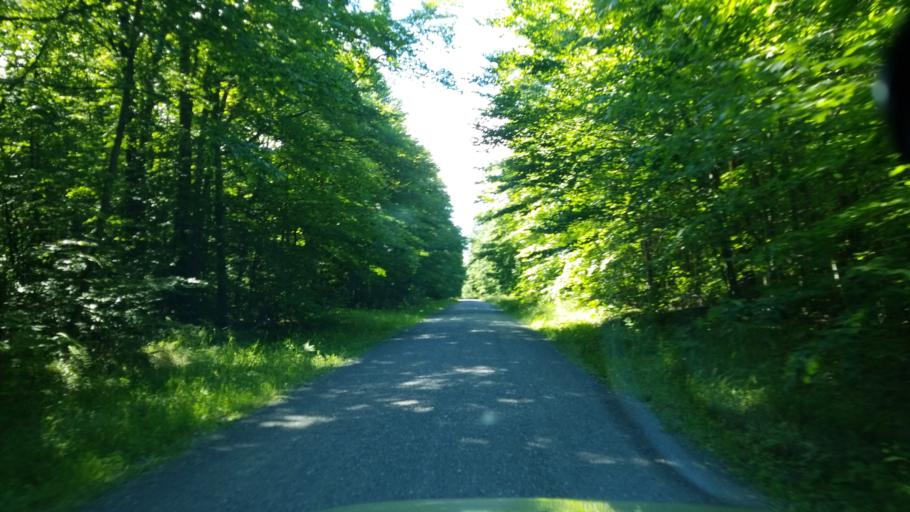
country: US
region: Pennsylvania
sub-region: Clearfield County
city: Clearfield
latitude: 41.2042
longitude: -78.4870
